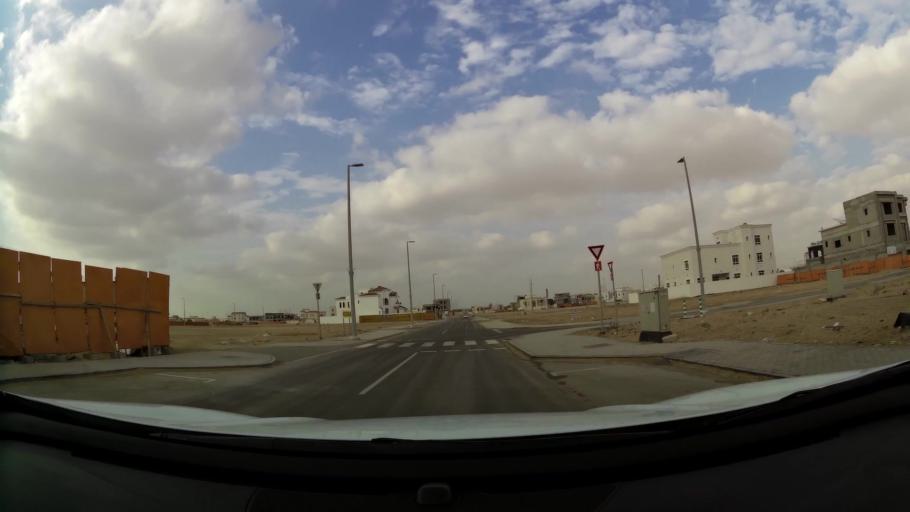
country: AE
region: Abu Dhabi
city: Abu Dhabi
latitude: 24.3278
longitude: 54.5772
